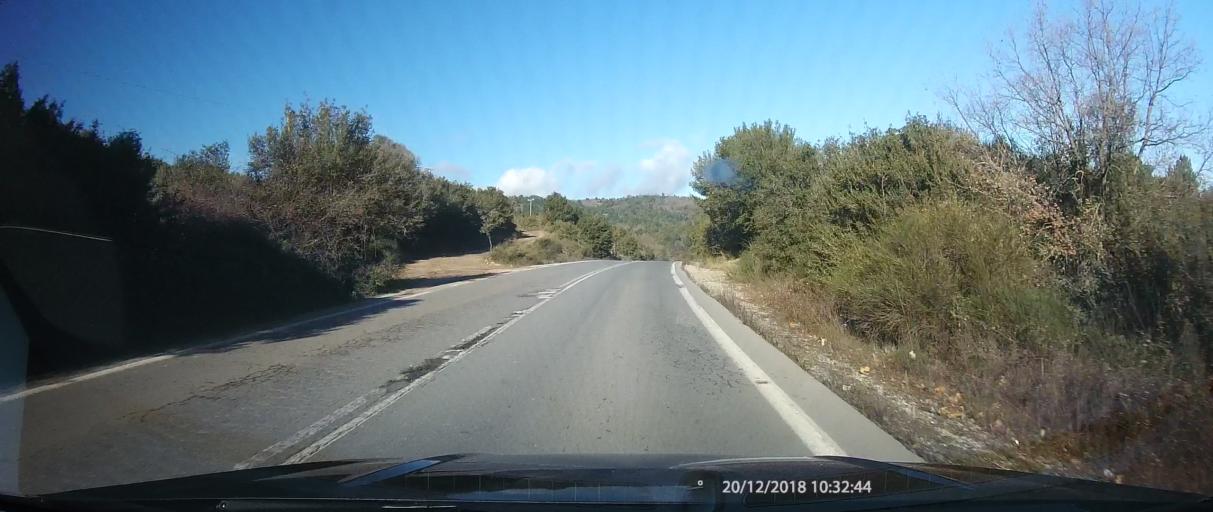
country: GR
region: Peloponnese
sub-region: Nomos Lakonias
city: Kariai
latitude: 37.3300
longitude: 22.4215
